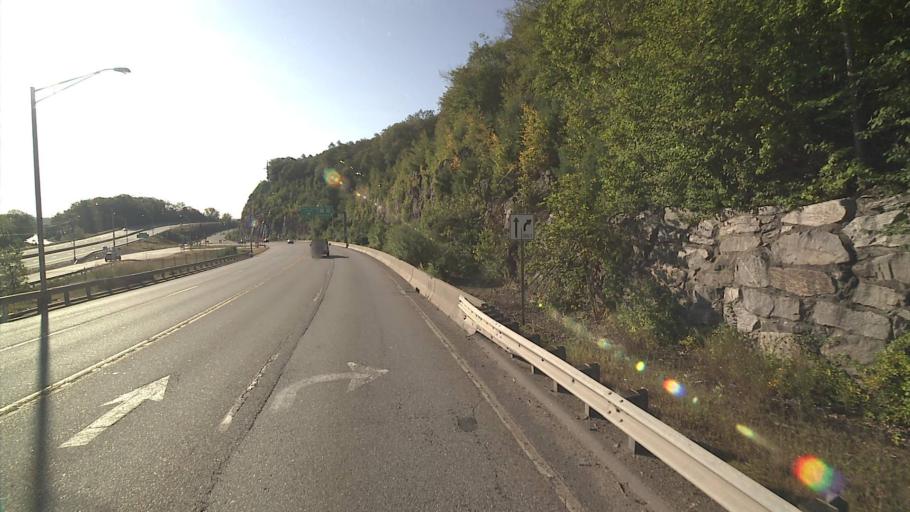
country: US
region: Connecticut
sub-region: New London County
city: Norwich
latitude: 41.5586
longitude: -72.1245
